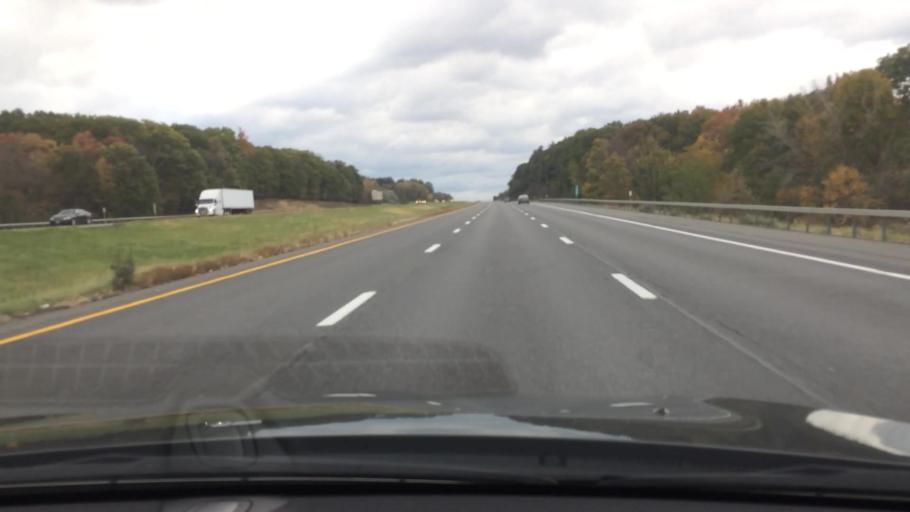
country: US
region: New York
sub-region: Rensselaer County
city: East Greenbush
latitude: 42.6155
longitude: -73.6894
